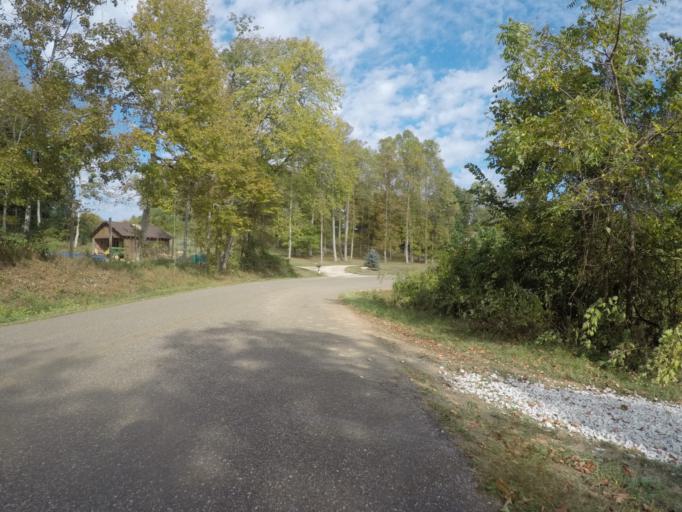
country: US
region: West Virginia
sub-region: Cabell County
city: Lesage
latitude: 38.5759
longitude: -82.4300
